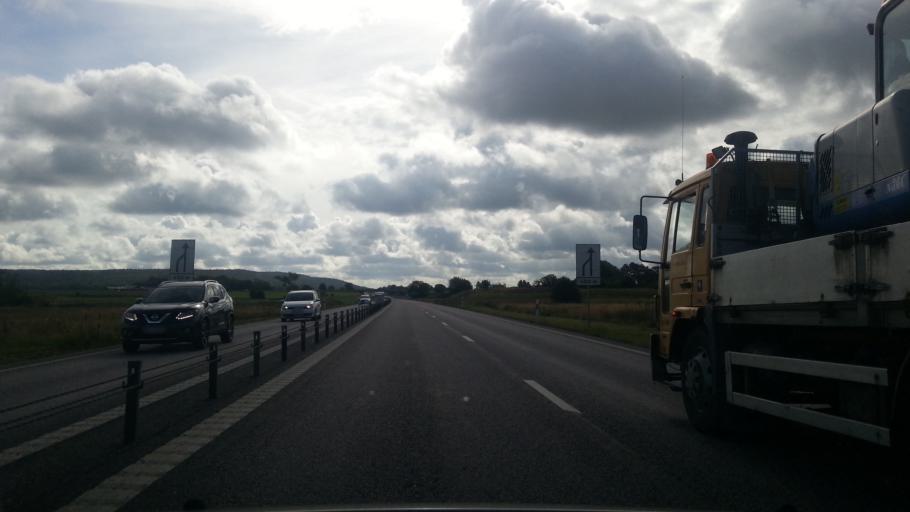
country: SE
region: Vaestra Goetaland
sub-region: Vanersborgs Kommun
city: Vargon
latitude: 58.2965
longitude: 12.3562
